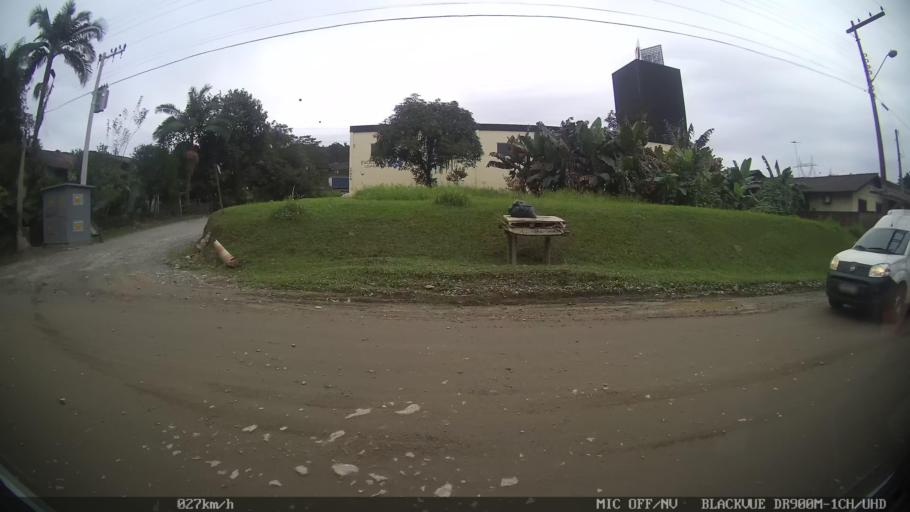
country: BR
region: Santa Catarina
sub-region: Joinville
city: Joinville
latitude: -26.2784
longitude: -48.8906
